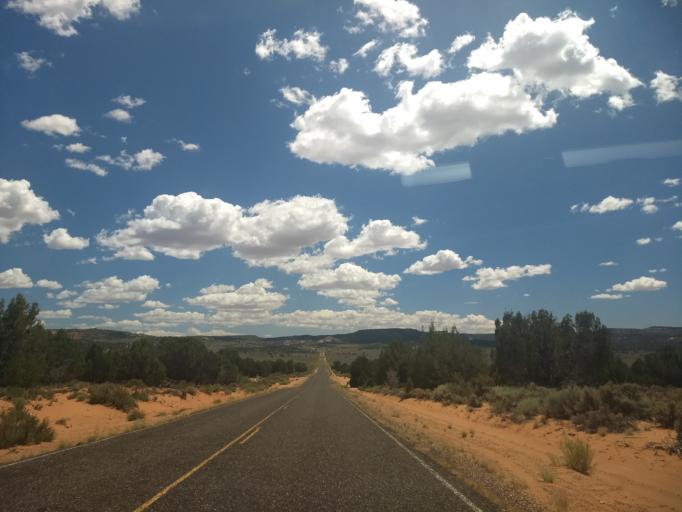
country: US
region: Utah
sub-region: Kane County
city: Kanab
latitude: 37.1728
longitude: -112.6612
